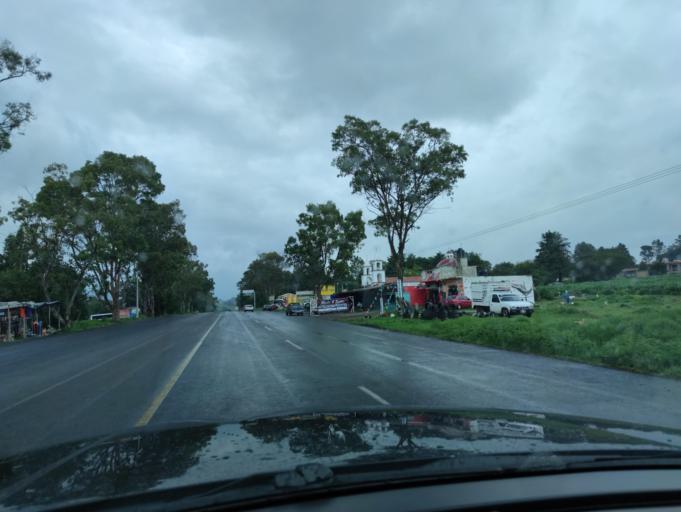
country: MX
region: Mexico
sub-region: Jilotepec
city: Doxhicho
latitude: 19.9134
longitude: -99.6043
